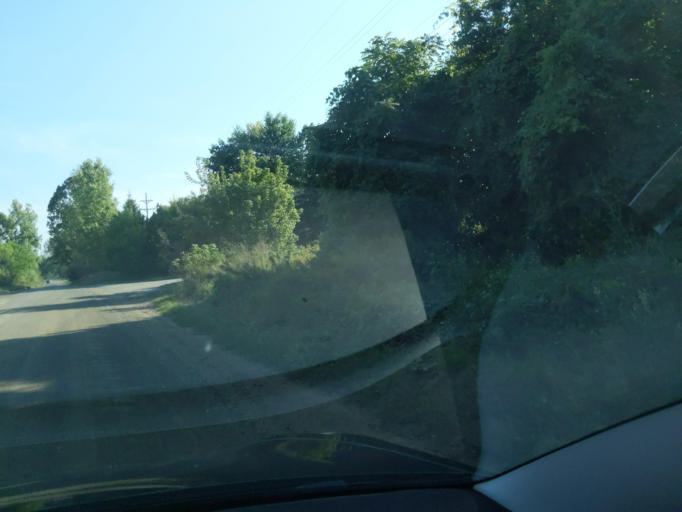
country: US
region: Michigan
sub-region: Oakland County
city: South Lyon
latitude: 42.4587
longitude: -83.6666
